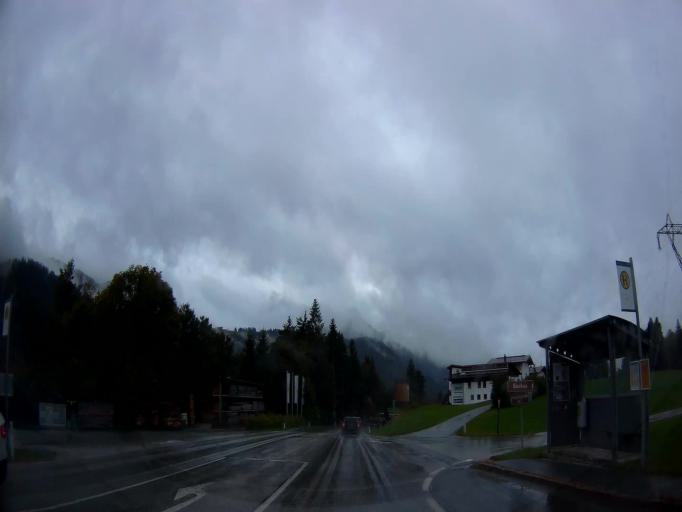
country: AT
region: Tyrol
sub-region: Politischer Bezirk Kitzbuhel
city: Fieberbrunn
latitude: 47.4689
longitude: 12.5678
